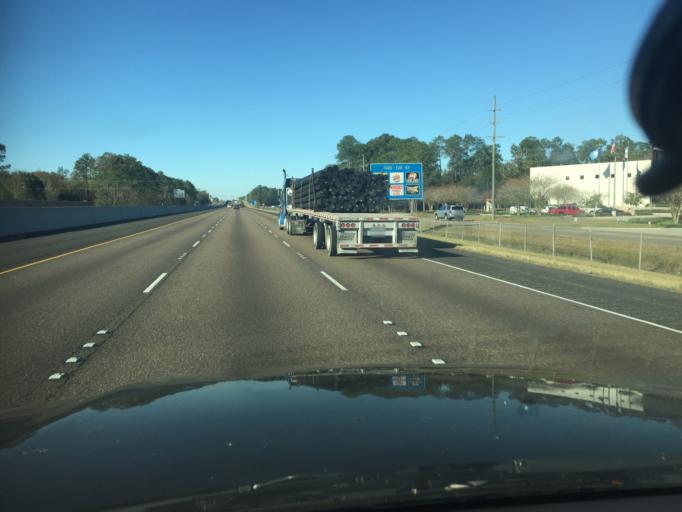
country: US
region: Louisiana
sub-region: Saint Tammany Parish
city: Slidell
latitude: 30.3102
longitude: -89.7599
